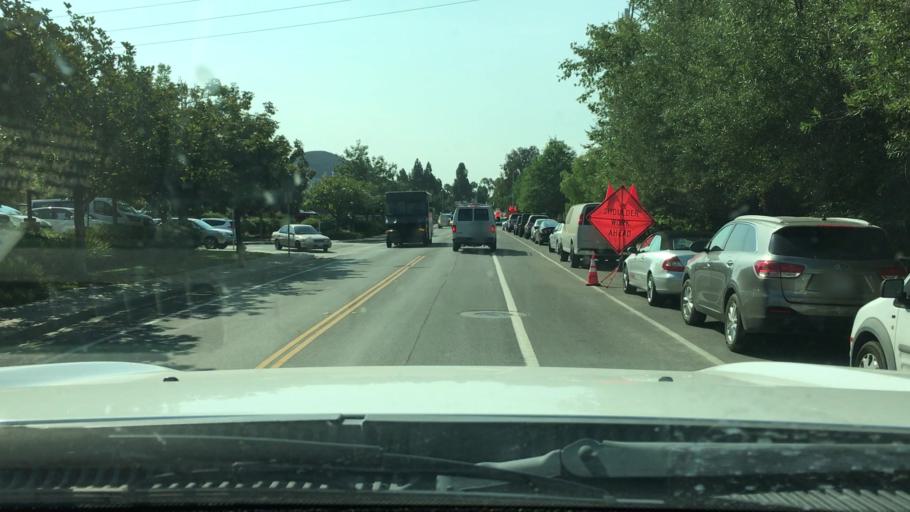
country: US
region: California
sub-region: San Luis Obispo County
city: San Luis Obispo
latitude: 35.2565
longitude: -120.6437
